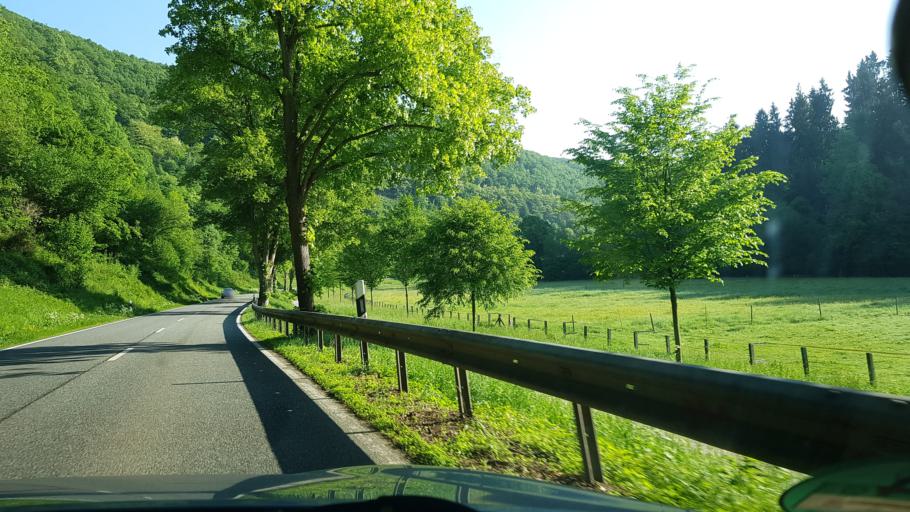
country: DE
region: Rheinland-Pfalz
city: Eitelborn
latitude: 50.3650
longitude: 7.7306
